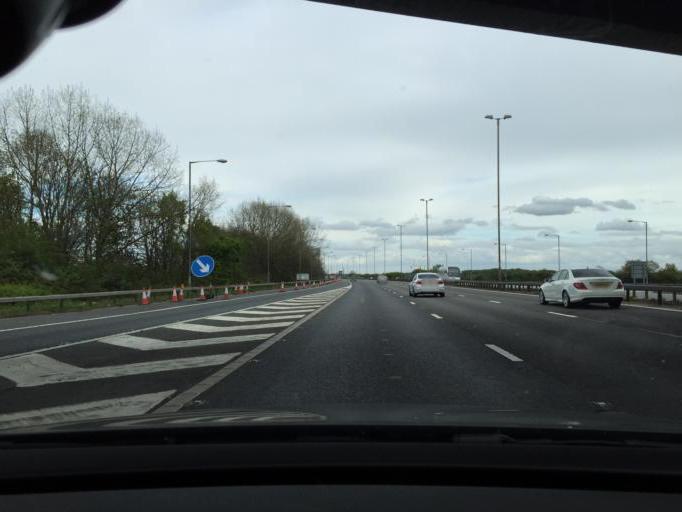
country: GB
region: England
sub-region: West Berkshire
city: Calcot
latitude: 51.4235
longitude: -1.0308
